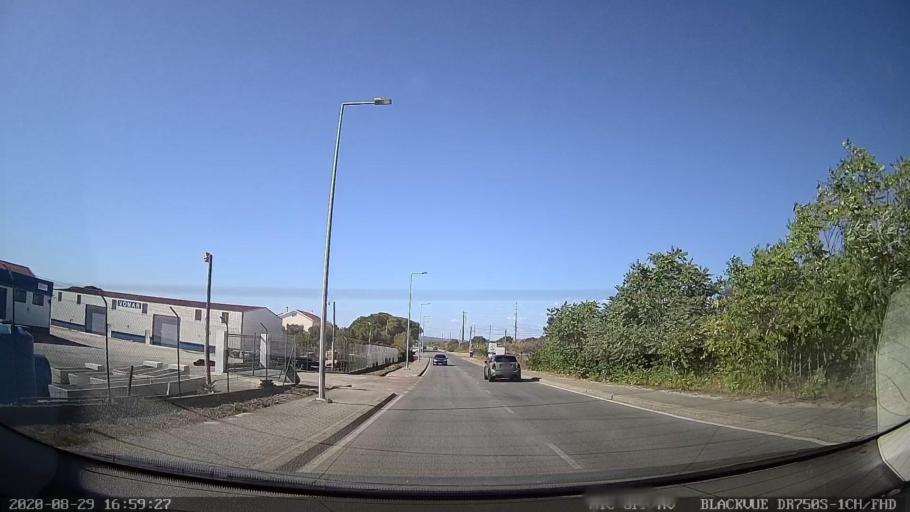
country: PT
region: Setubal
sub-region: Alcacer do Sal
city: Alcacer do Sal
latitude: 38.3868
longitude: -8.5130
